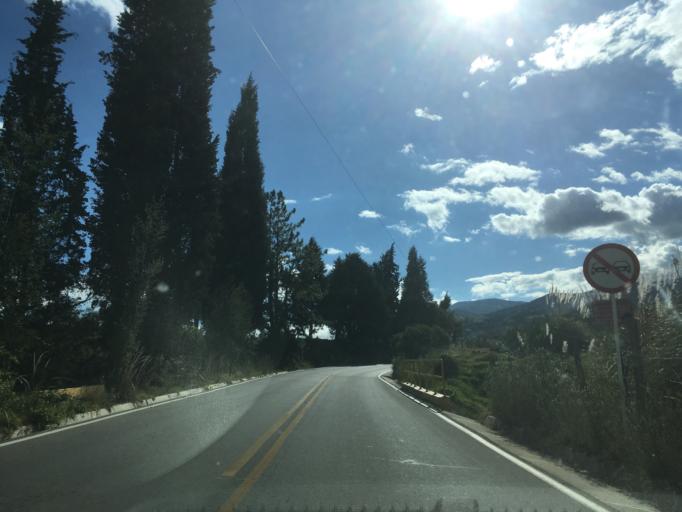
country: CO
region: Boyaca
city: Pesca
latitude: 5.6013
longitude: -73.0254
